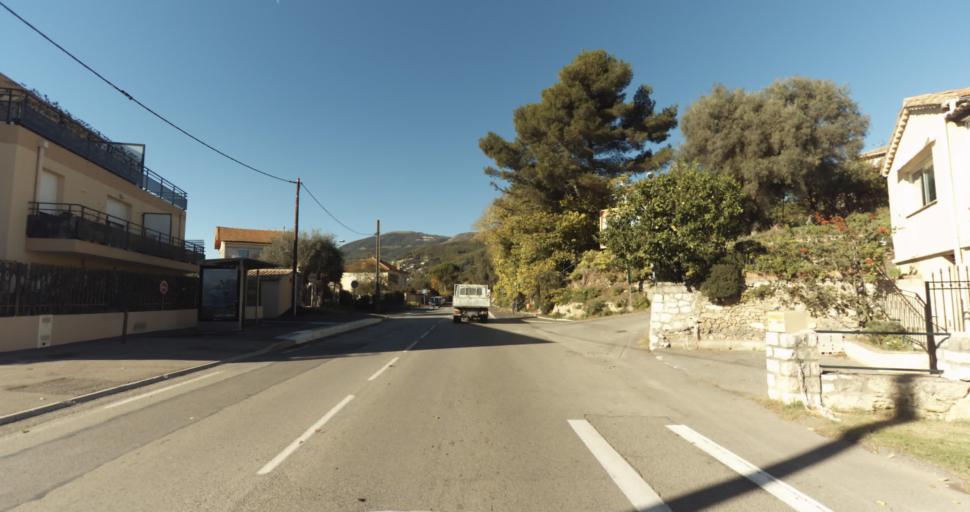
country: FR
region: Provence-Alpes-Cote d'Azur
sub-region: Departement des Alpes-Maritimes
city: Vence
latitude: 43.7245
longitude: 7.1007
